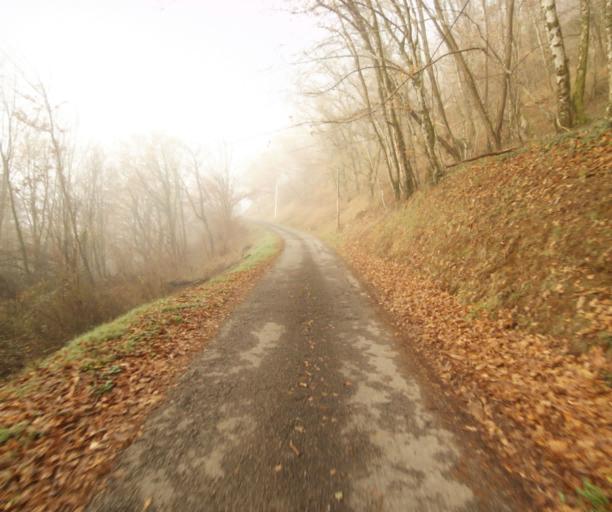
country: FR
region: Limousin
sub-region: Departement de la Correze
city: Laguenne
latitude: 45.2620
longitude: 1.7881
